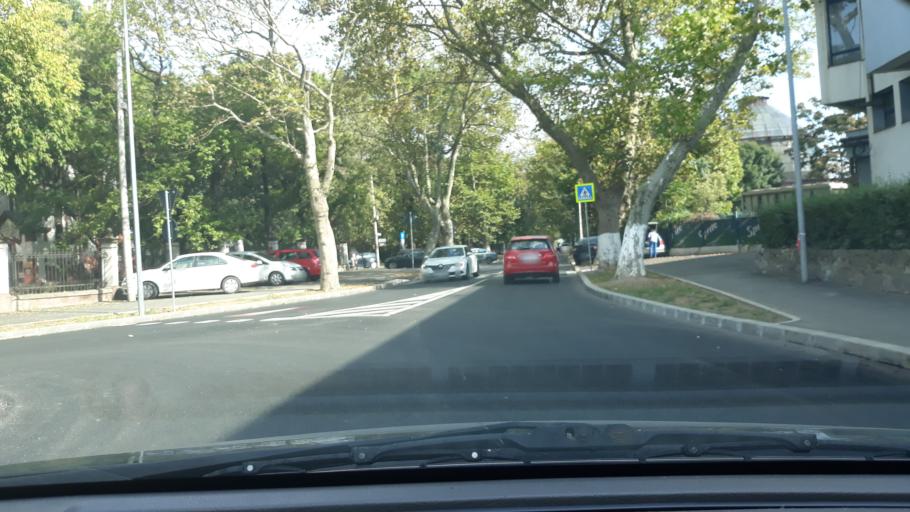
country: RO
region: Bihor
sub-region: Comuna Biharea
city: Oradea
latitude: 47.0557
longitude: 21.9426
